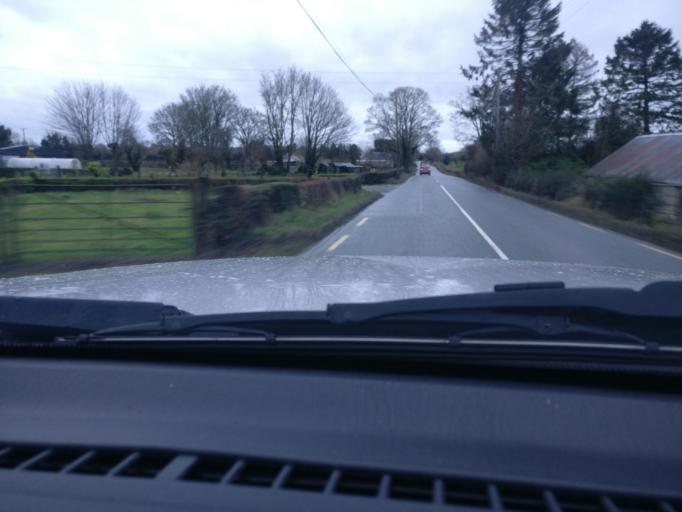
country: IE
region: Leinster
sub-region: An Mhi
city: Longwood
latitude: 53.4992
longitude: -6.8568
